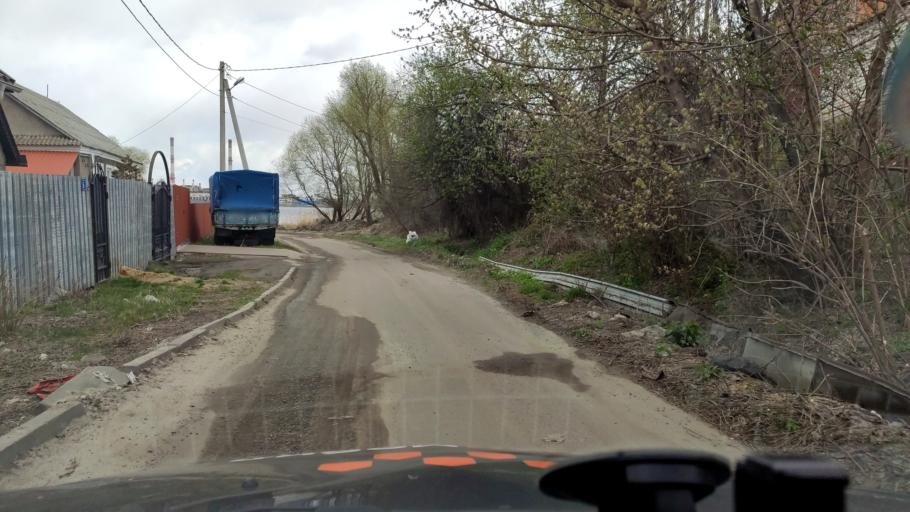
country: RU
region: Voronezj
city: Voronezh
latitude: 51.6289
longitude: 39.2003
